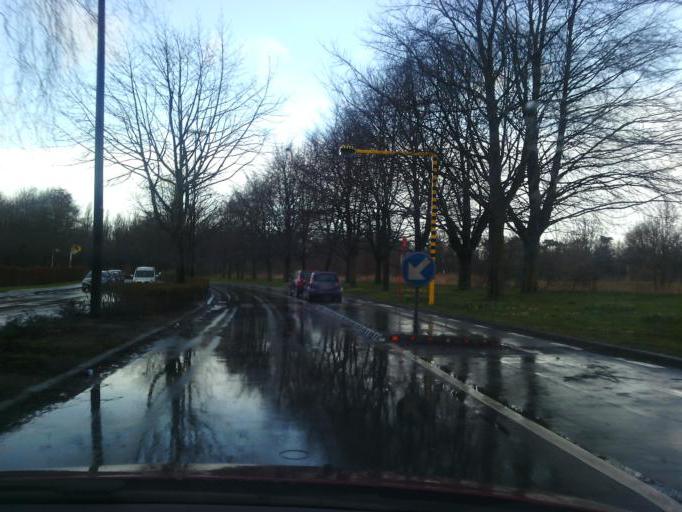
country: BE
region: Flanders
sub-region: Provincie Oost-Vlaanderen
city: Lokeren
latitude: 51.1068
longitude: 3.9974
